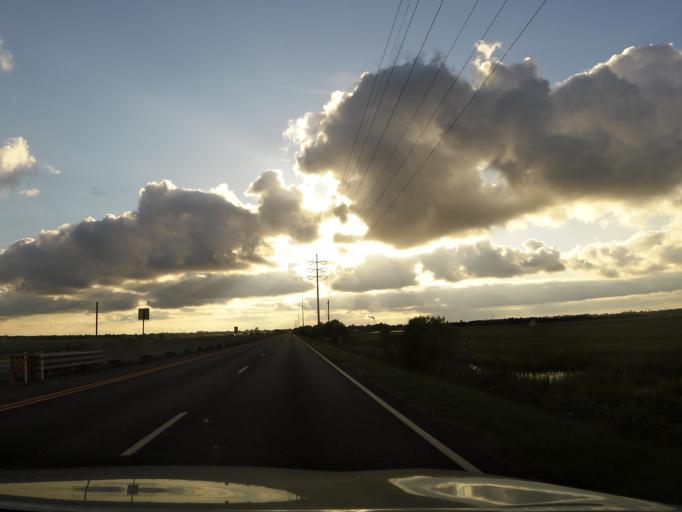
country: US
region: Georgia
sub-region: Glynn County
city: Brunswick
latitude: 31.1629
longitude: -81.4543
